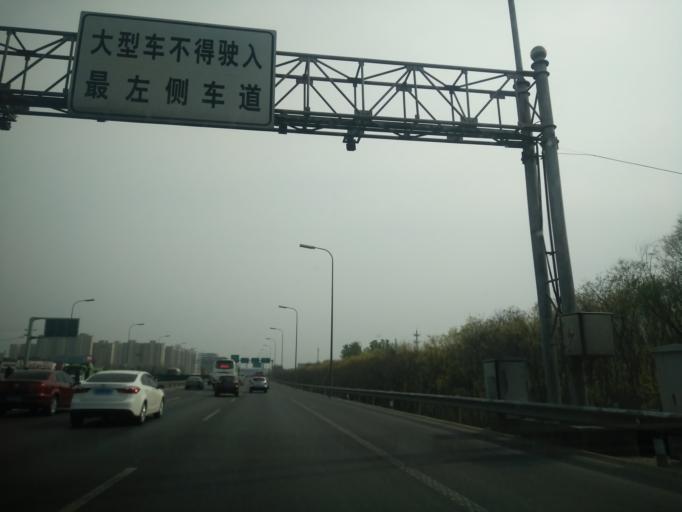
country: CN
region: Beijing
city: Dongfeng
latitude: 39.8616
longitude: 116.5422
